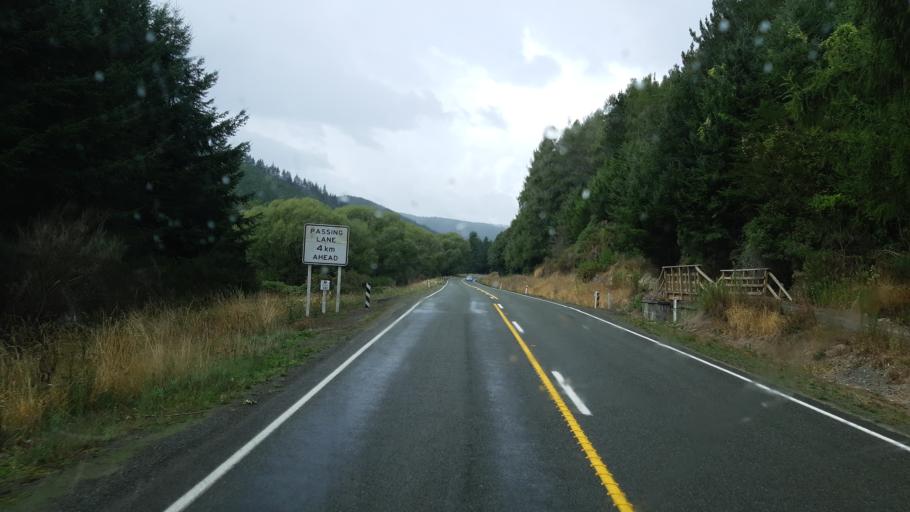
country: NZ
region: Tasman
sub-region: Tasman District
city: Wakefield
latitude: -41.4757
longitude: 172.8545
